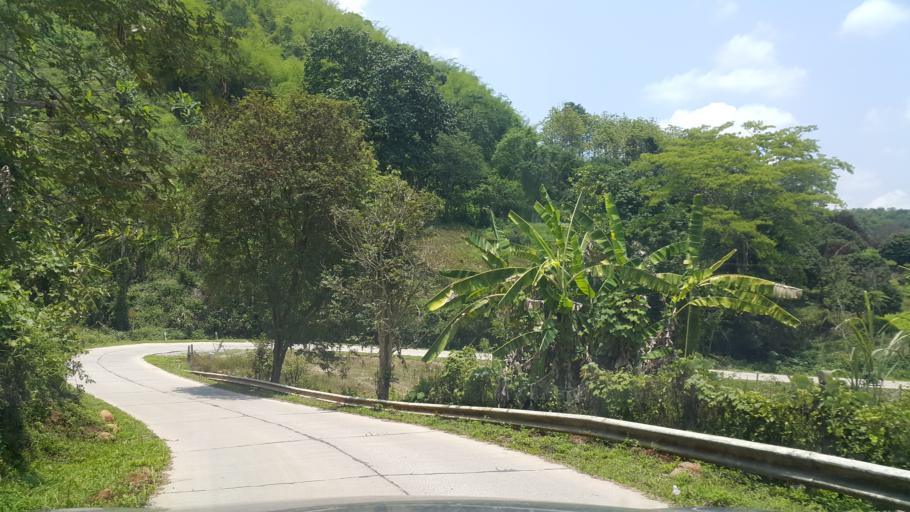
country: TH
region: Chiang Rai
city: Chiang Rai
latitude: 19.9763
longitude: 99.7474
